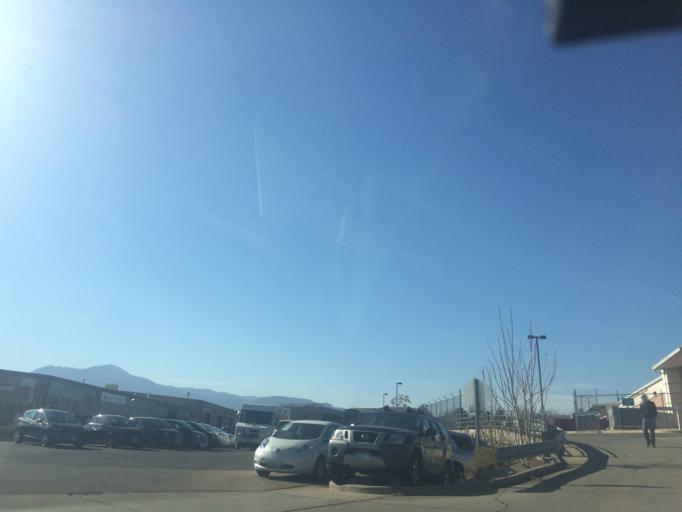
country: US
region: Colorado
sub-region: Boulder County
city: Boulder
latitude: 40.0284
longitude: -105.2256
